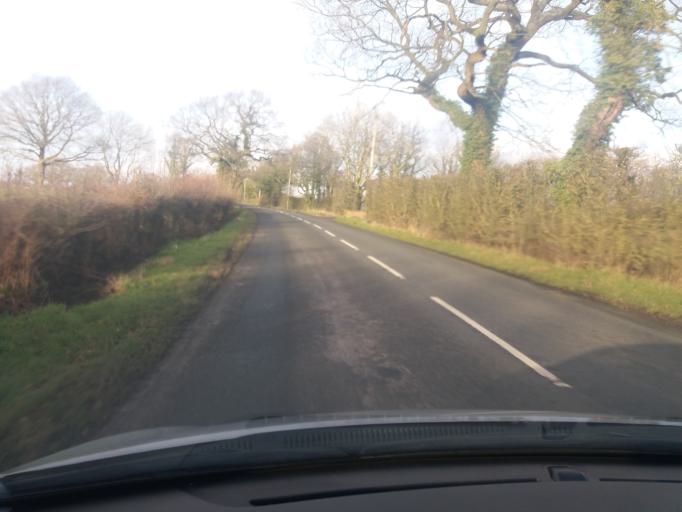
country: GB
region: England
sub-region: Lancashire
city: Euxton
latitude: 53.6663
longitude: -2.7137
